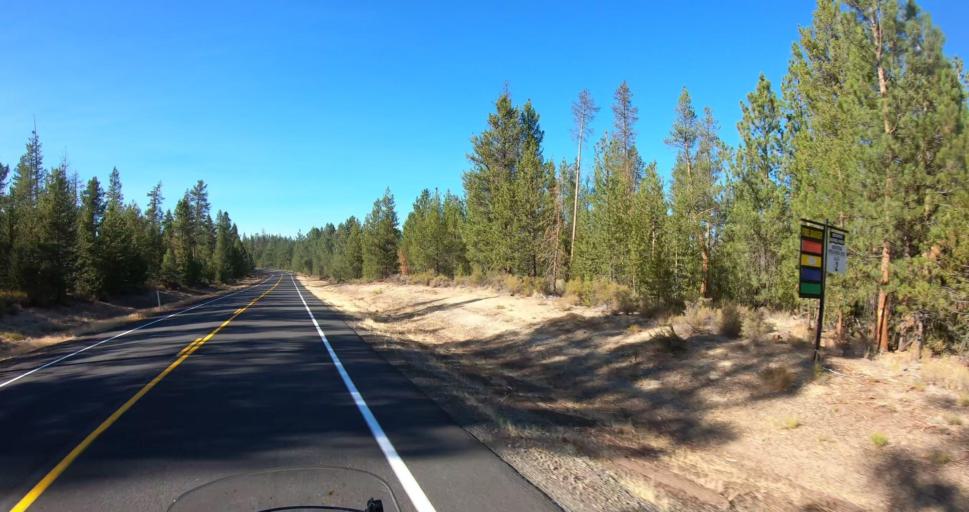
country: US
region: Oregon
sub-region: Deschutes County
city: La Pine
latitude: 43.4645
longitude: -121.3855
